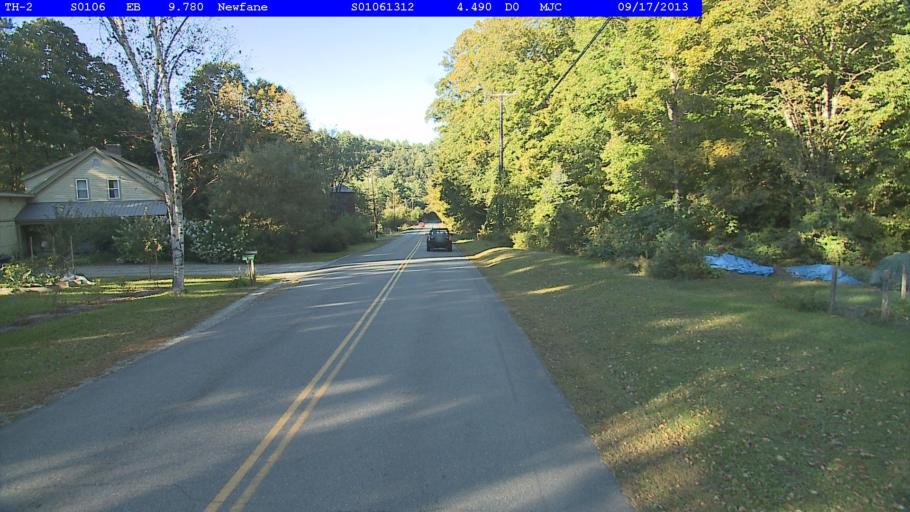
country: US
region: Vermont
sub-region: Windham County
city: Newfane
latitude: 42.9390
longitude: -72.6916
